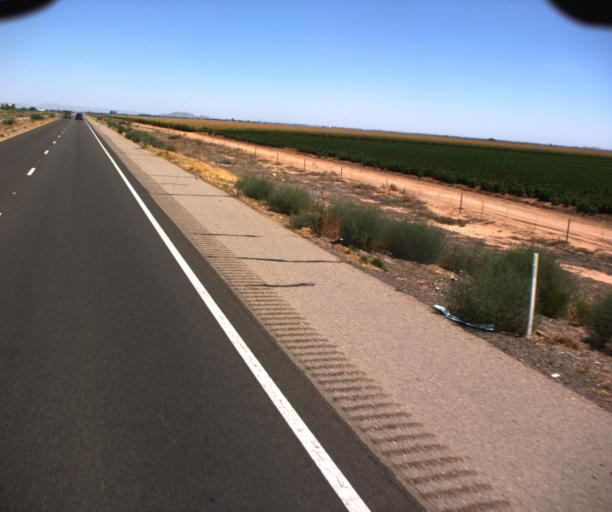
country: US
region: Arizona
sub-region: Pinal County
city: Maricopa
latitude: 33.0059
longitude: -112.0478
